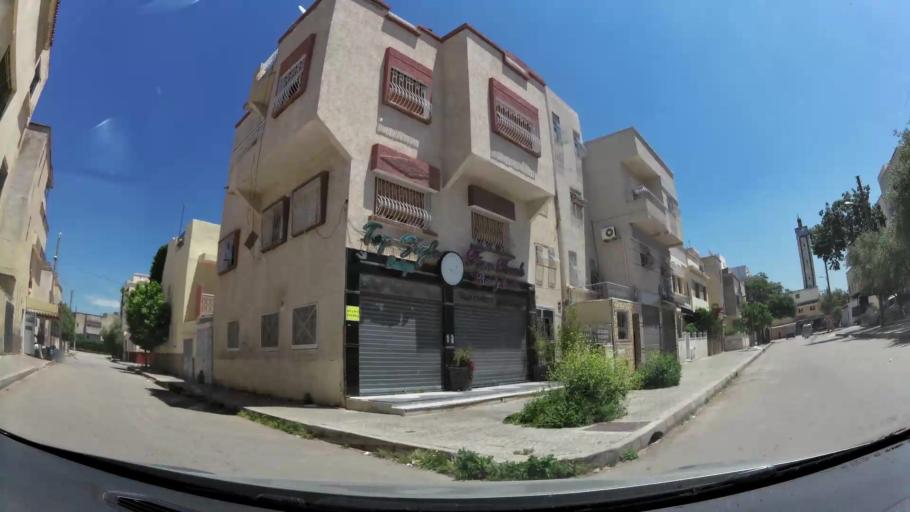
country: MA
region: Fes-Boulemane
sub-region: Fes
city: Fes
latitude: 34.0265
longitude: -5.0077
